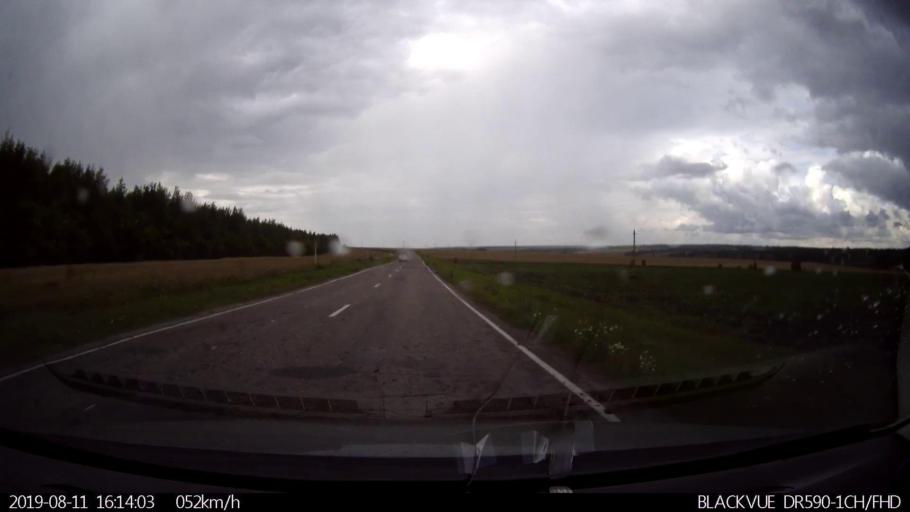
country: RU
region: Ulyanovsk
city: Ignatovka
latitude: 54.0249
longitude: 47.6350
